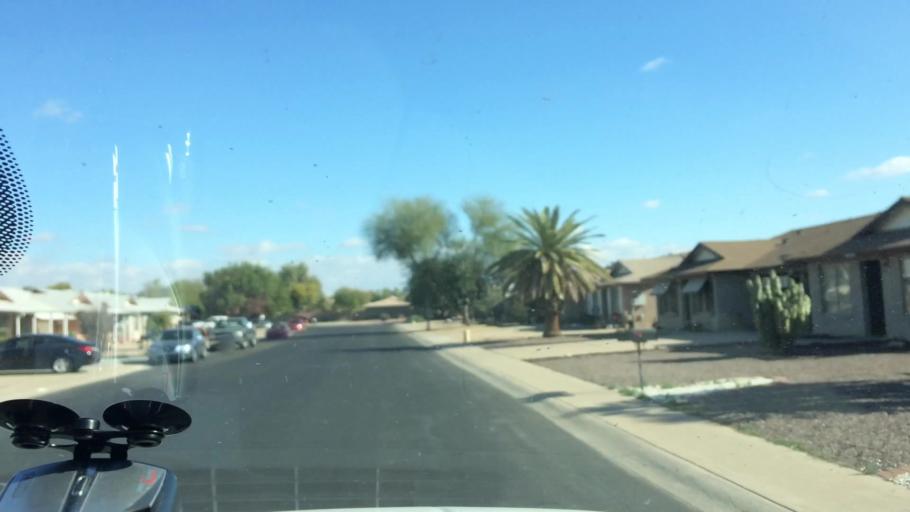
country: US
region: Arizona
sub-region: Maricopa County
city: Sun City
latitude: 33.5730
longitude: -112.2656
